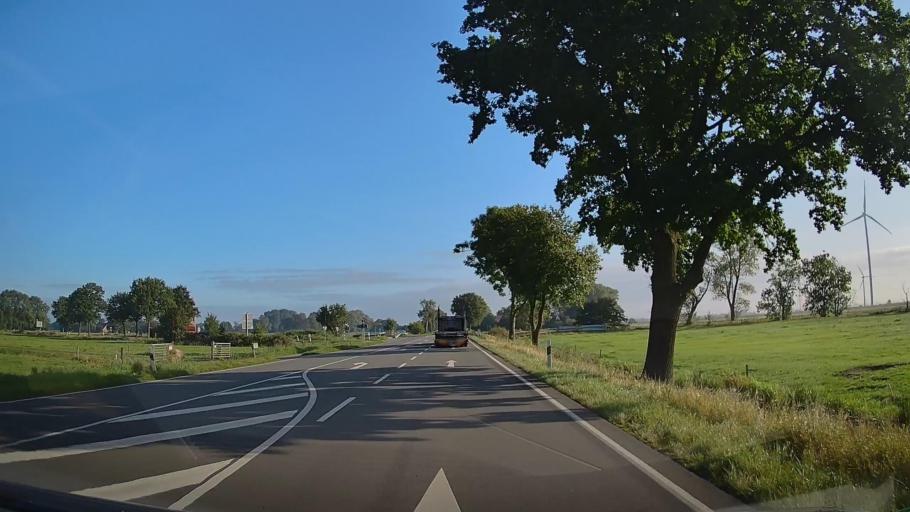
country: DE
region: Lower Saxony
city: Ovelgonne
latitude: 53.2805
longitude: 8.3685
